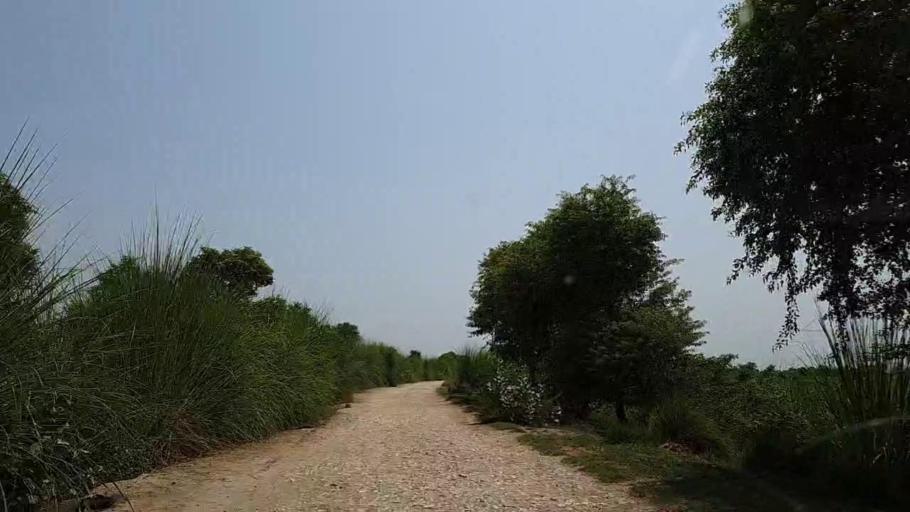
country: PK
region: Sindh
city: Adilpur
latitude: 27.9398
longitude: 69.3961
